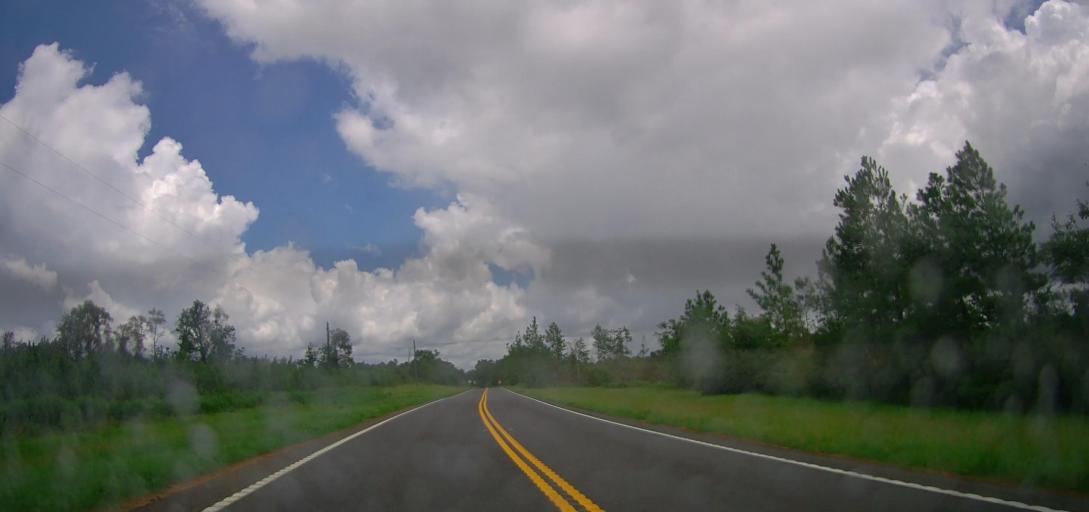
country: US
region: Georgia
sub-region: Pulaski County
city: Hawkinsville
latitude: 32.1644
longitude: -83.5459
